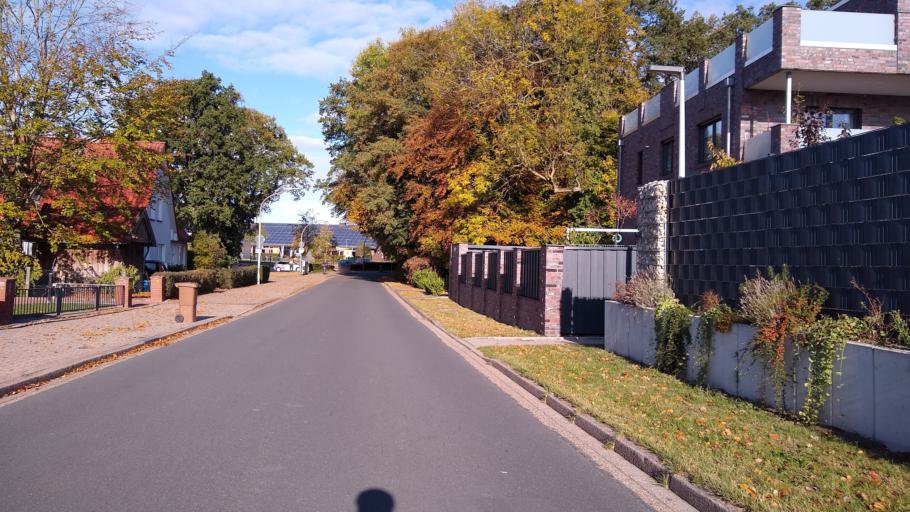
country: DE
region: Lower Saxony
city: Rastede
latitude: 53.2393
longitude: 8.1967
